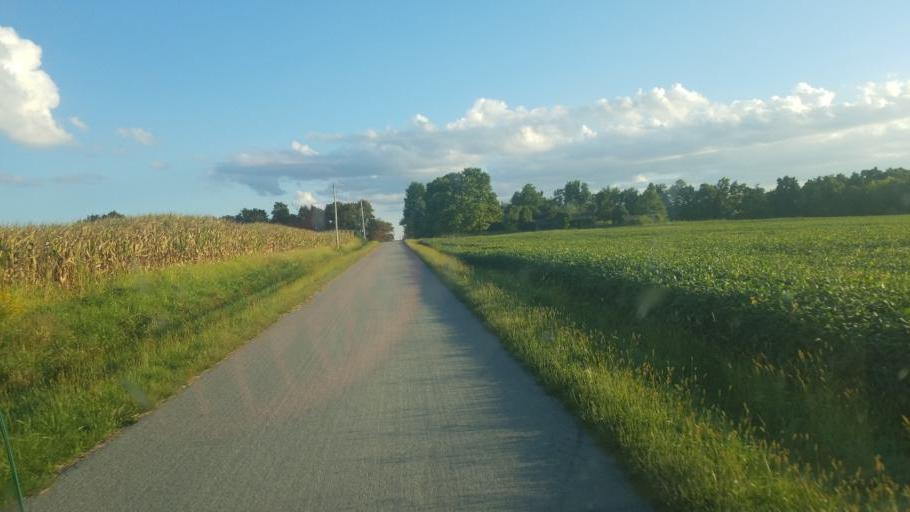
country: US
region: Ohio
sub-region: Wyandot County
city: Upper Sandusky
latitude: 40.8573
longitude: -83.1507
